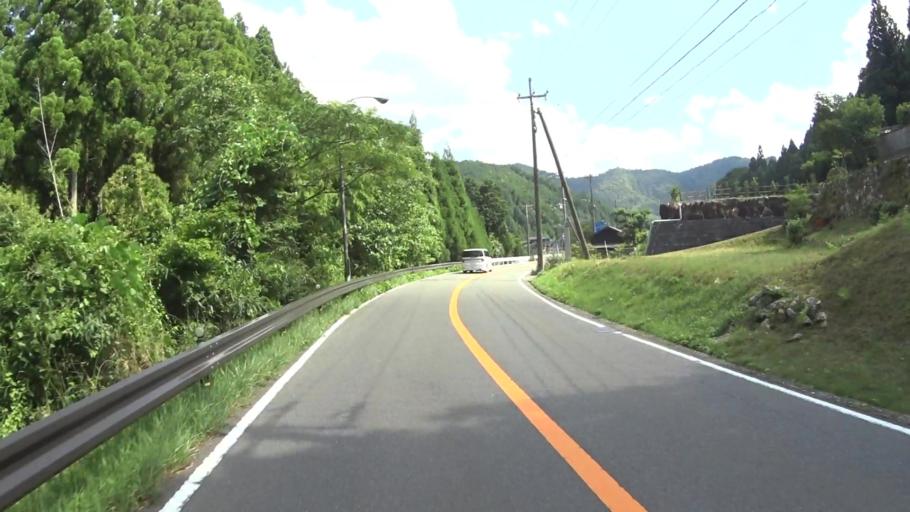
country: JP
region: Kyoto
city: Maizuru
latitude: 35.2847
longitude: 135.5530
